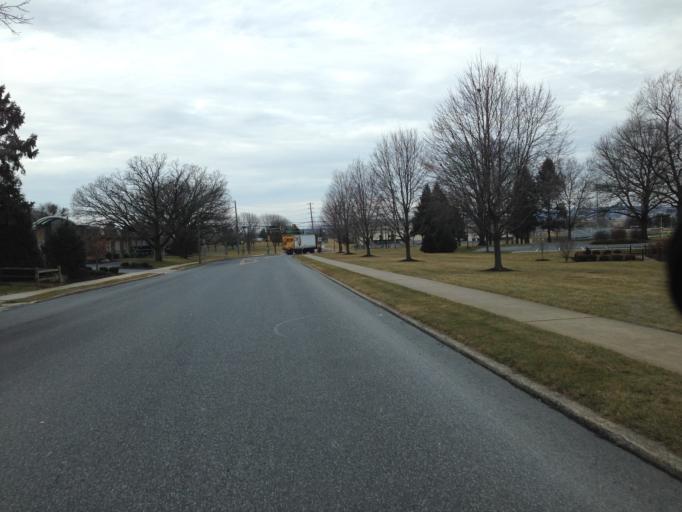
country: US
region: Pennsylvania
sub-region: Lancaster County
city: Lititz
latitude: 40.1526
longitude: -76.3148
